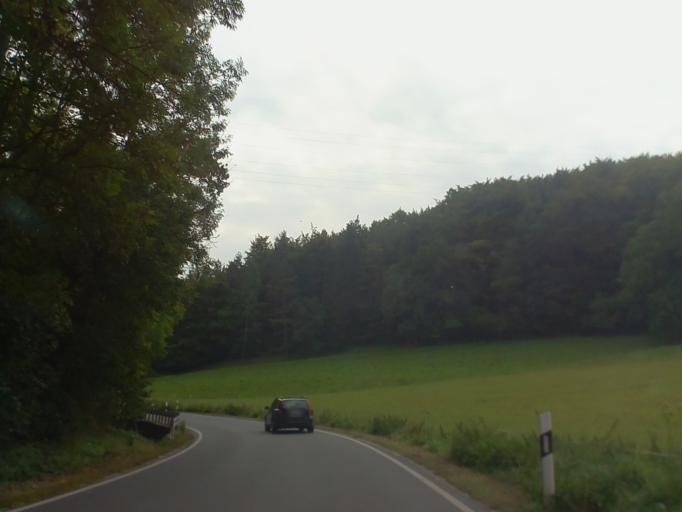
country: DE
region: Thuringia
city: Bucha
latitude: 50.8869
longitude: 11.5399
